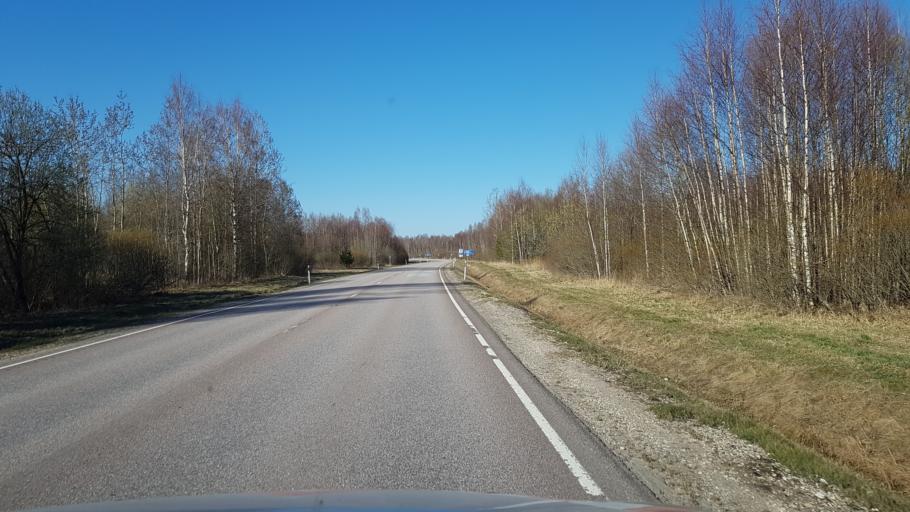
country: EE
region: Jogevamaa
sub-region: Mustvee linn
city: Mustvee
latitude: 58.8218
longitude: 26.9369
